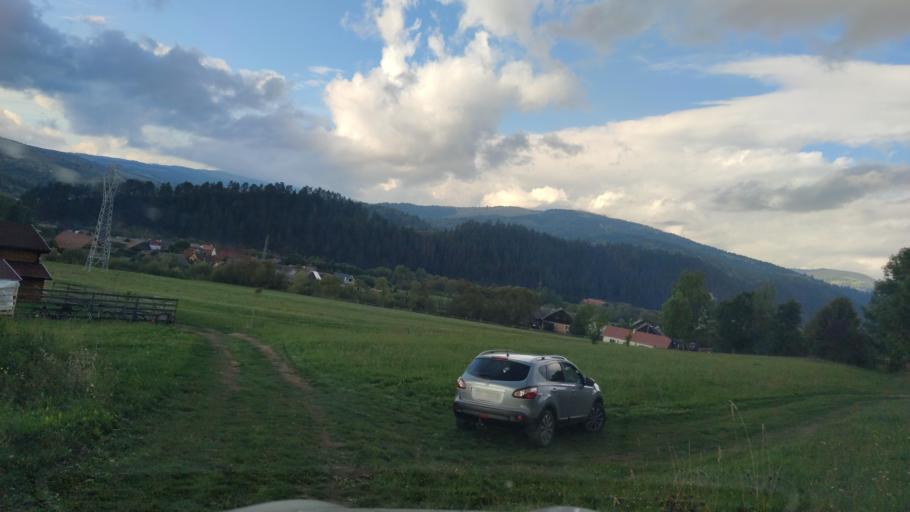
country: RO
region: Harghita
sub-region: Municipiul Gheorgheni
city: Gheorgheni
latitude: 46.7213
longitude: 25.6364
